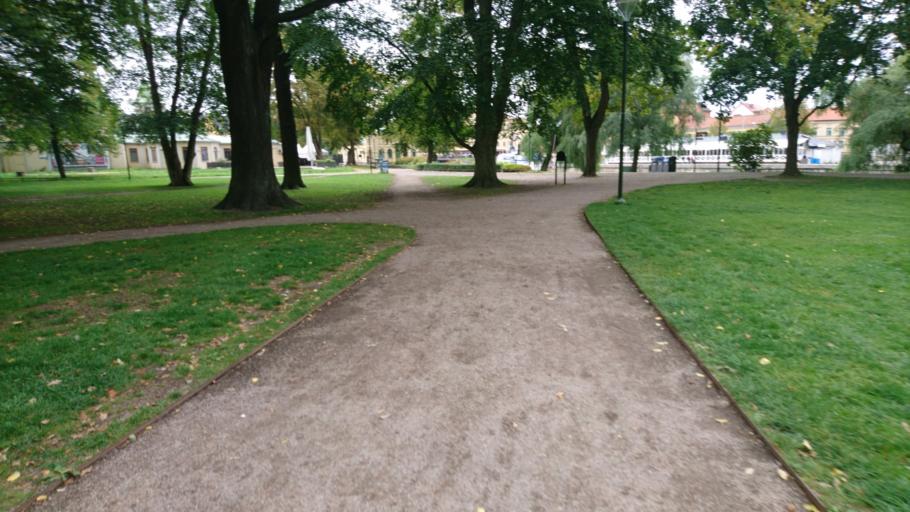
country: SE
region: Uppsala
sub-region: Uppsala Kommun
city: Uppsala
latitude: 59.8532
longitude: 17.6420
